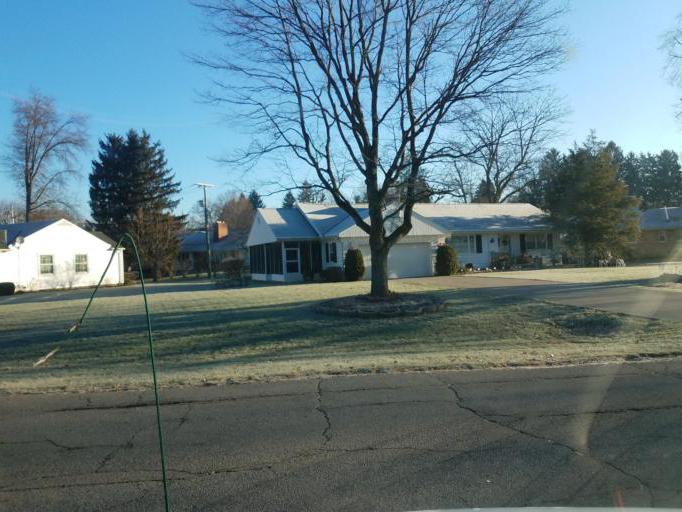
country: US
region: Ohio
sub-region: Marion County
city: Marion
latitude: 40.5731
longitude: -83.1149
